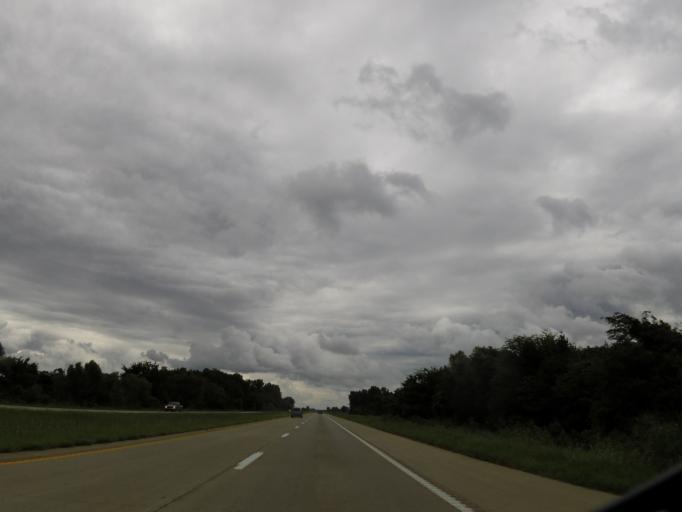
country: US
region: Missouri
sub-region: Mississippi County
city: Charleston
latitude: 36.9491
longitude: -89.2860
